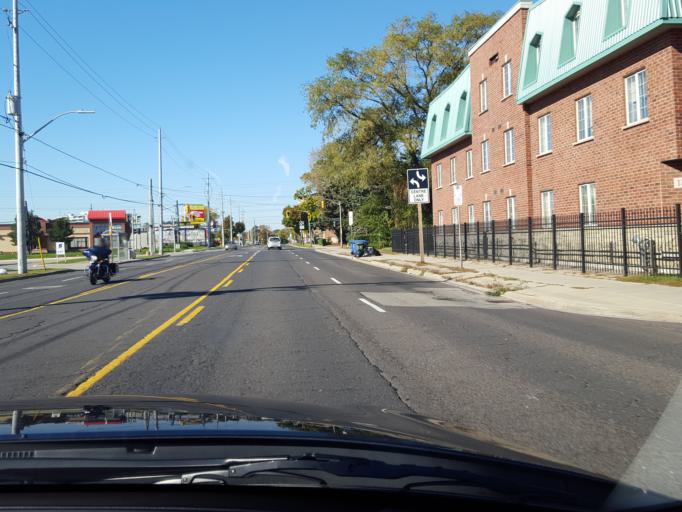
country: CA
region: Ontario
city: Ancaster
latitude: 43.2576
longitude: -79.9291
